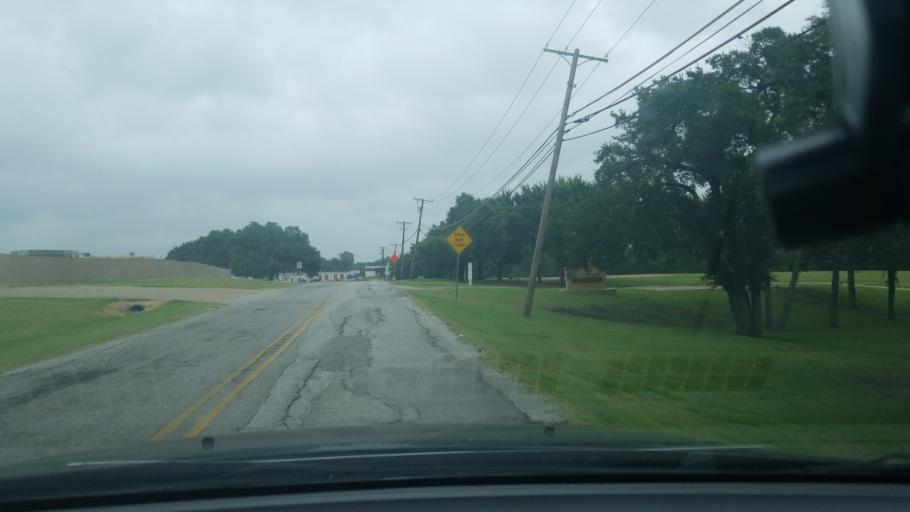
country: US
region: Texas
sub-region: Dallas County
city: Mesquite
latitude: 32.7905
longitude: -96.6502
